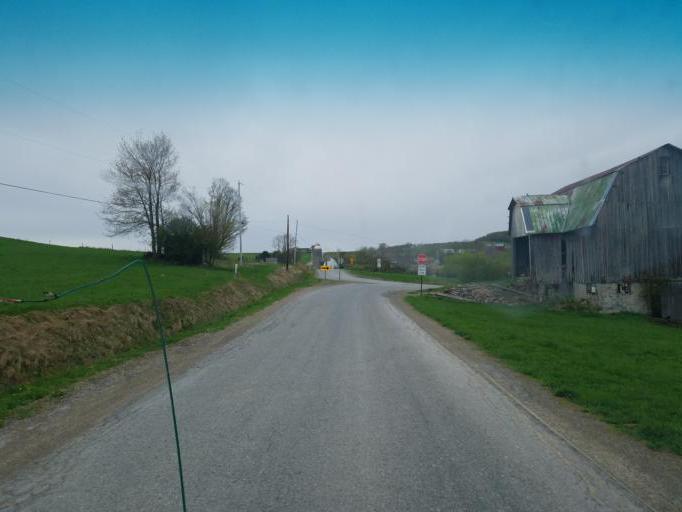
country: US
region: Pennsylvania
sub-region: Potter County
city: Galeton
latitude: 41.8881
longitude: -77.7397
